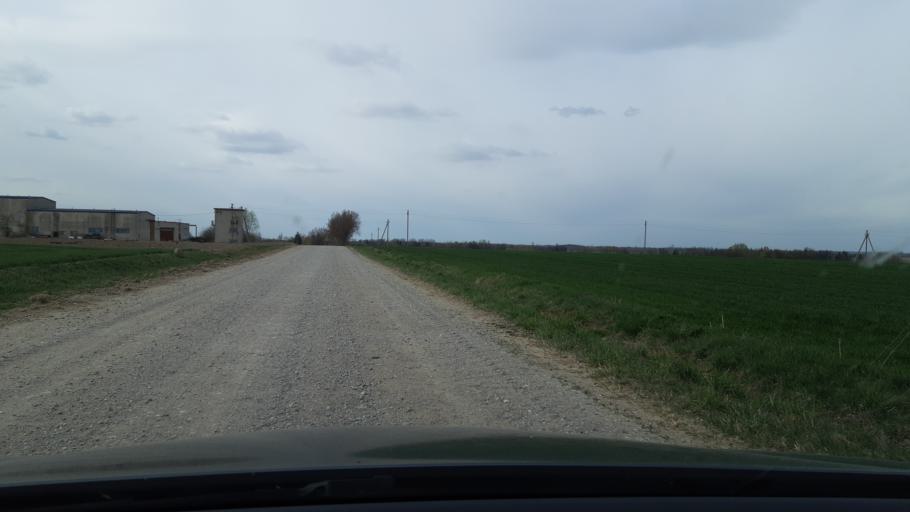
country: LT
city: Virbalis
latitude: 54.6158
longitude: 22.8430
